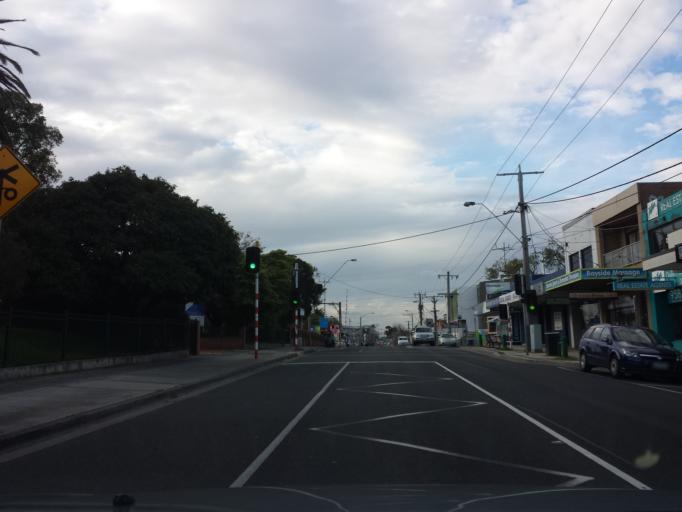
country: AU
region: Victoria
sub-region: Bayside
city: Cheltenham
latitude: -37.9687
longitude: 145.0551
